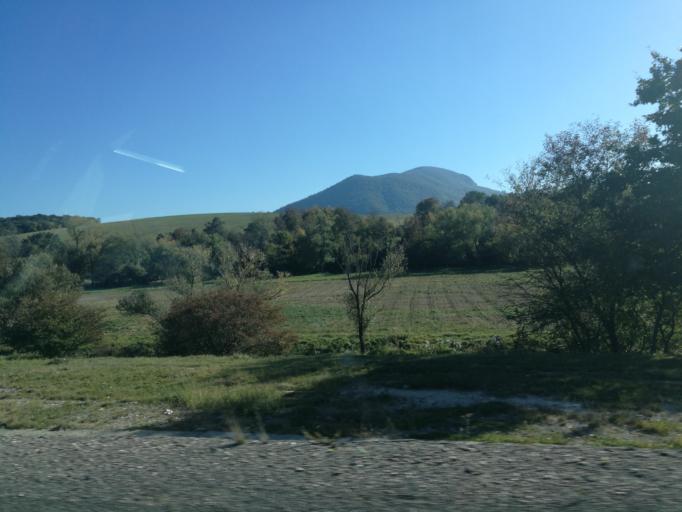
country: RO
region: Brasov
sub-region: Comuna Dumbravita
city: Dumbravita
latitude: 45.7580
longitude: 25.3959
